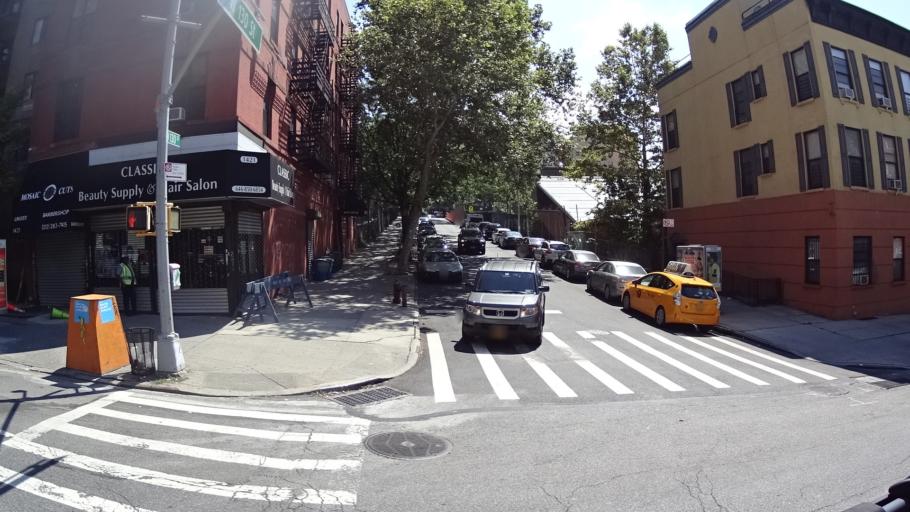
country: US
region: New Jersey
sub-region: Bergen County
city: Edgewater
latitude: 40.8158
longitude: -73.9545
